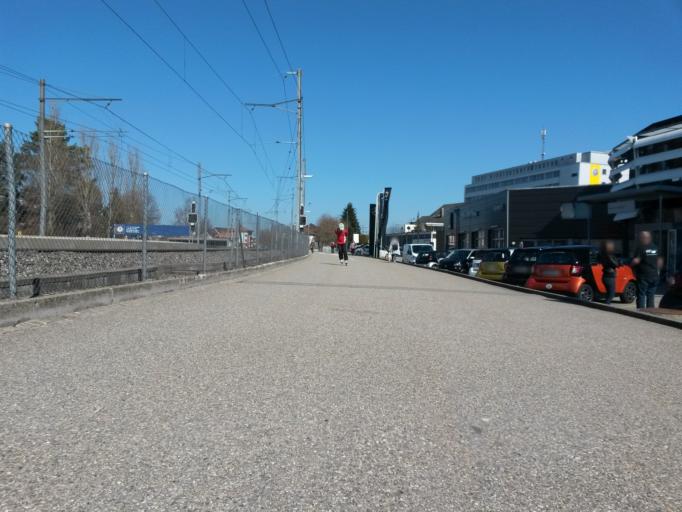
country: CH
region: Bern
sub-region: Bern-Mittelland District
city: Urtenen
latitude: 47.0186
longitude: 7.4942
